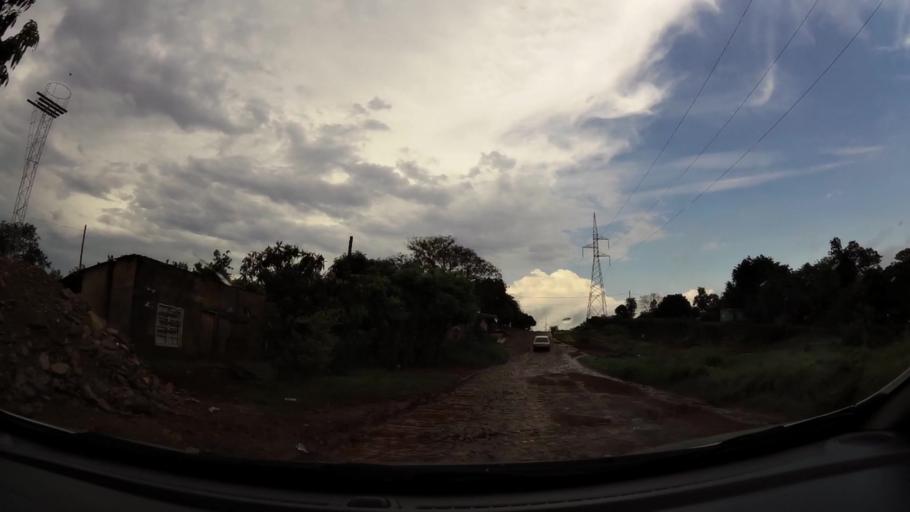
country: PY
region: Alto Parana
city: Presidente Franco
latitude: -25.5339
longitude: -54.6652
